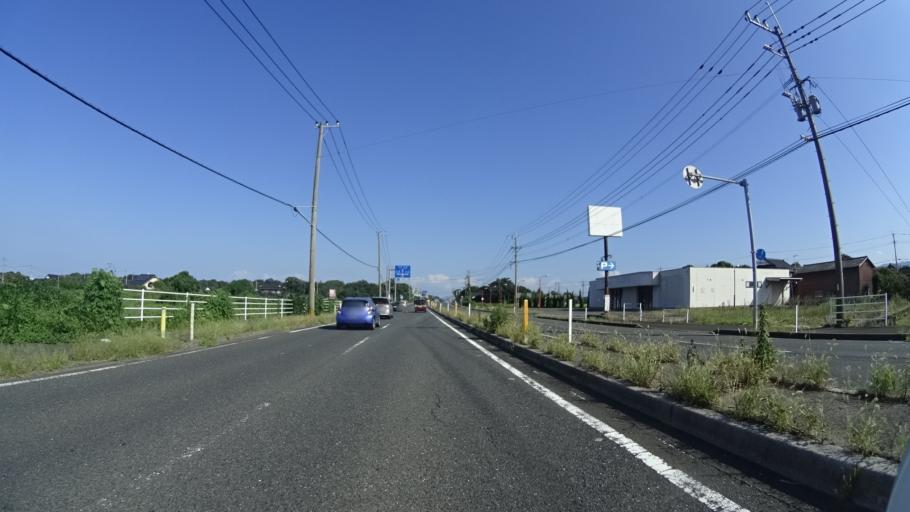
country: JP
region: Fukuoka
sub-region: Buzen-shi
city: Buzen
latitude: 33.5922
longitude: 131.1480
